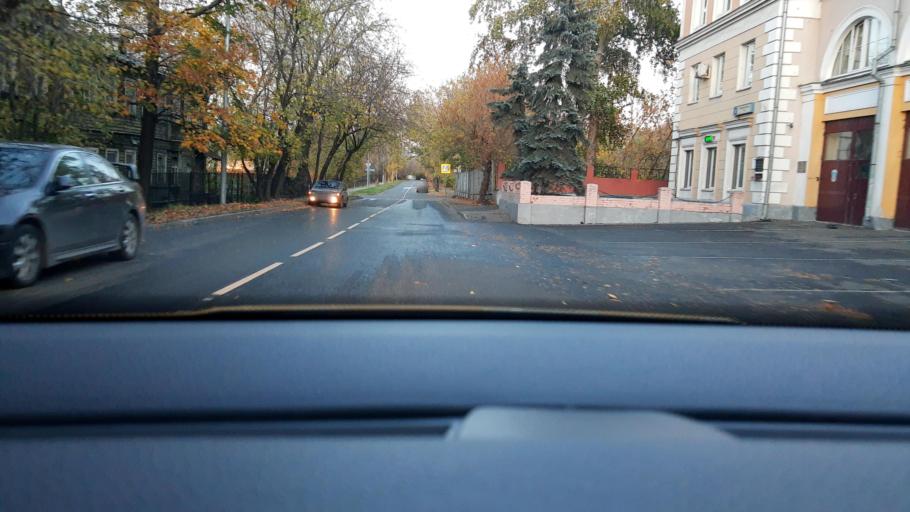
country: RU
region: Moscow
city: Likhobory
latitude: 55.8359
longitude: 37.5518
